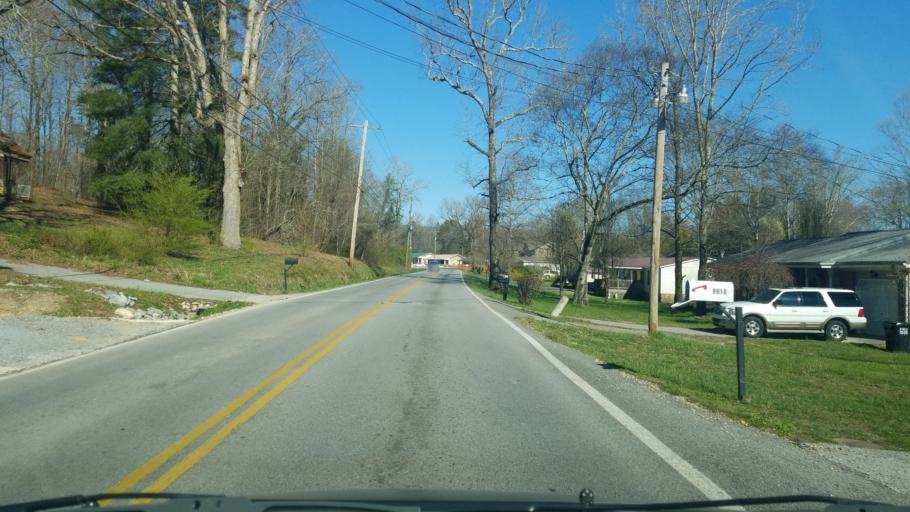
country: US
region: Tennessee
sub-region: Hamilton County
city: Middle Valley
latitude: 35.2120
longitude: -85.1748
